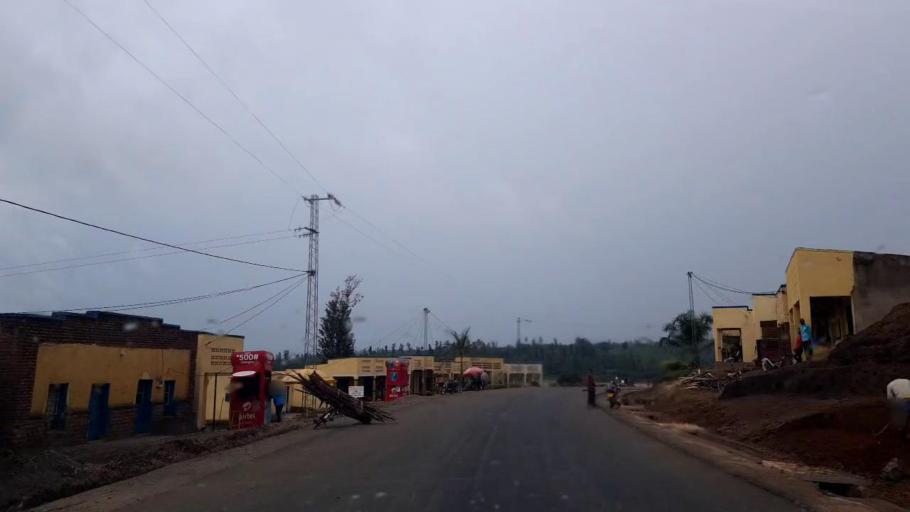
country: RW
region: Northern Province
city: Byumba
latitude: -1.4133
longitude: 30.2825
